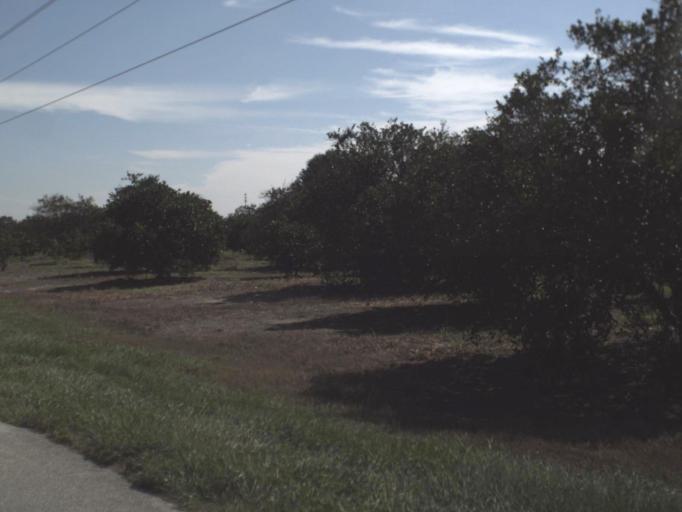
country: US
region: Florida
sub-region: Hardee County
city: Wauchula
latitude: 27.5554
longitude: -81.6884
